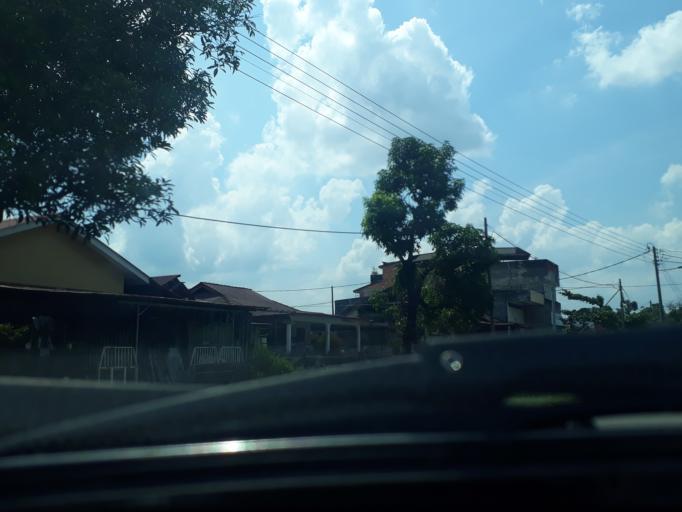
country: MY
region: Perak
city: Ipoh
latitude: 4.5775
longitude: 101.0850
